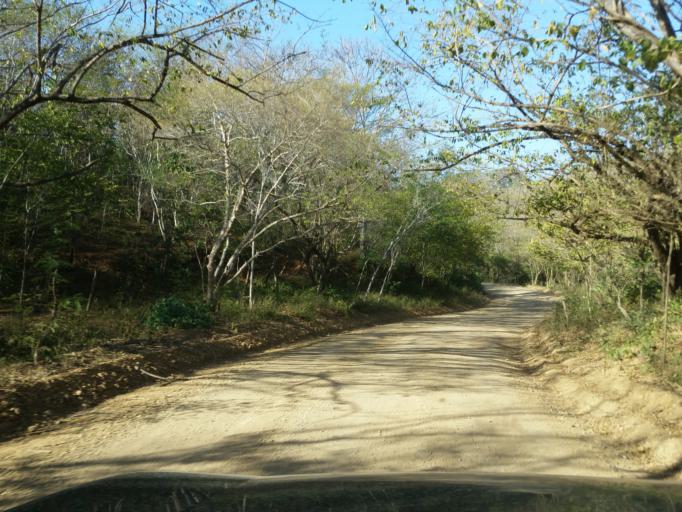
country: NI
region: Rivas
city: San Juan del Sur
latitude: 11.1698
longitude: -85.7970
